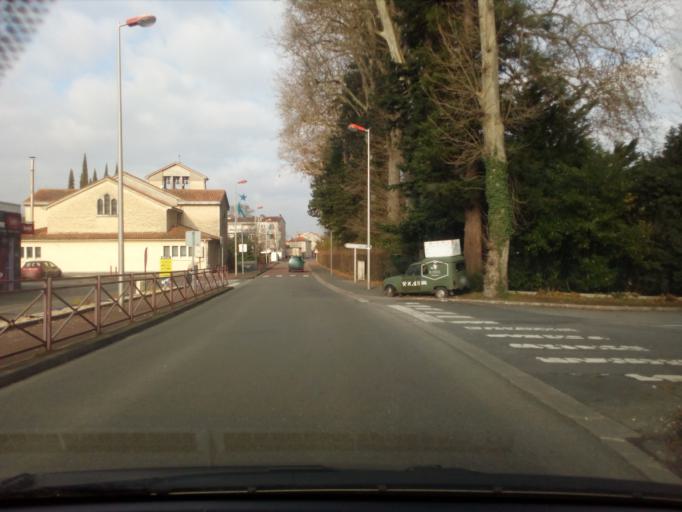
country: FR
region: Poitou-Charentes
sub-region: Departement de la Charente
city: Gond-Pontouvre
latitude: 45.6717
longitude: 0.1600
